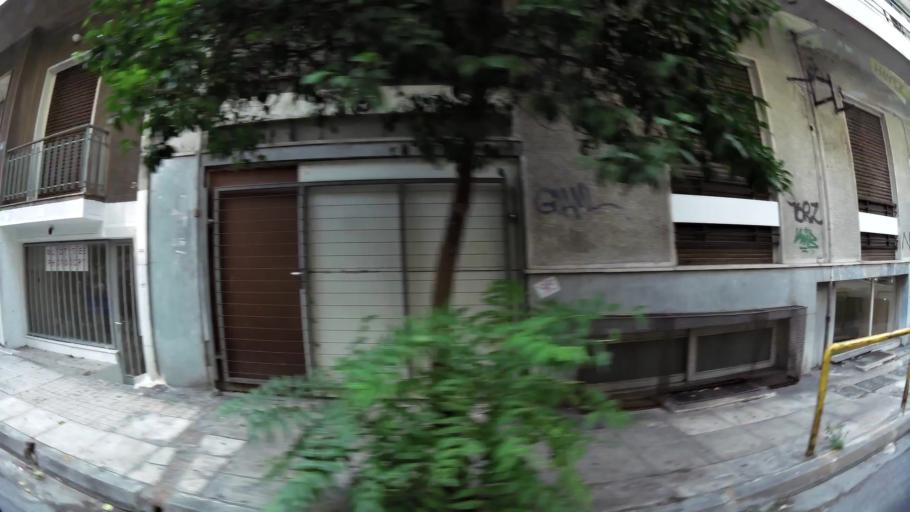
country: GR
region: Attica
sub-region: Nomarchia Athinas
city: Kipseli
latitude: 37.9962
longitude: 23.7389
